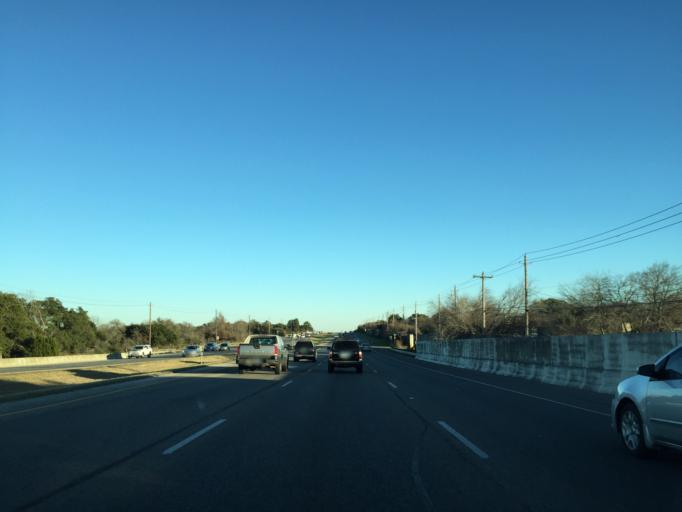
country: US
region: Texas
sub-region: Williamson County
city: Jollyville
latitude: 30.4315
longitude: -97.7271
